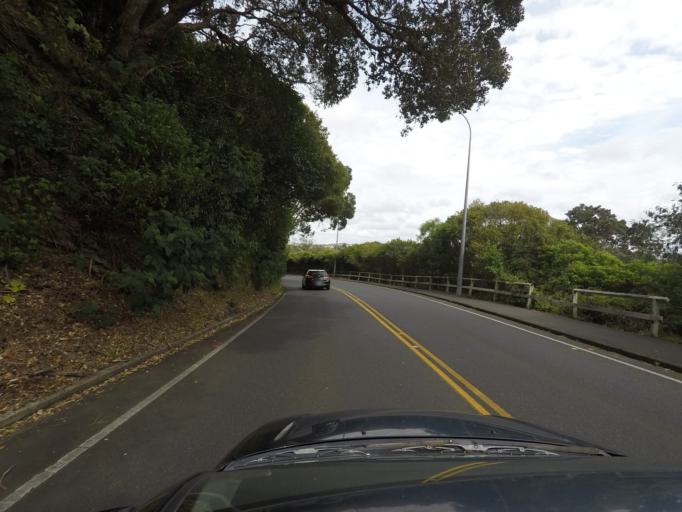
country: NZ
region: Auckland
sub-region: Auckland
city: Auckland
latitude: -36.8596
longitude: 174.8110
